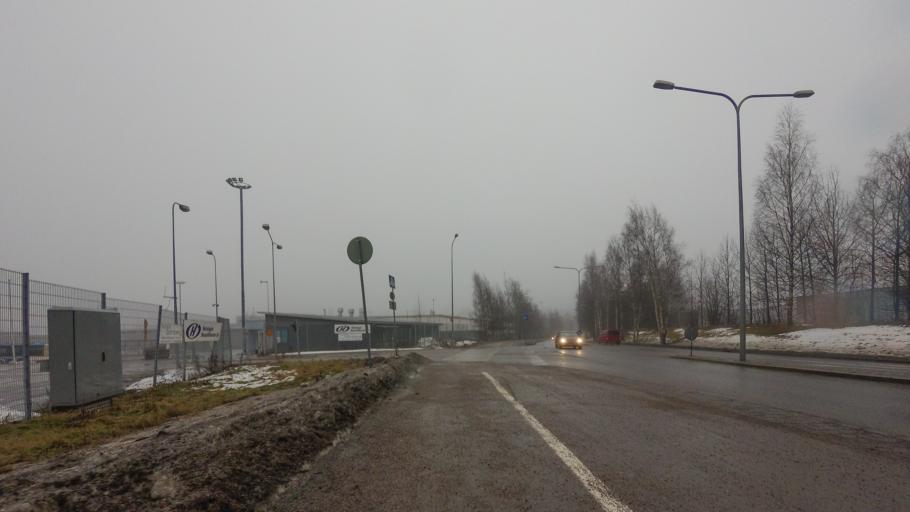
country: FI
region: Uusimaa
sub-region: Helsinki
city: Vantaa
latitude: 60.2127
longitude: 25.0599
